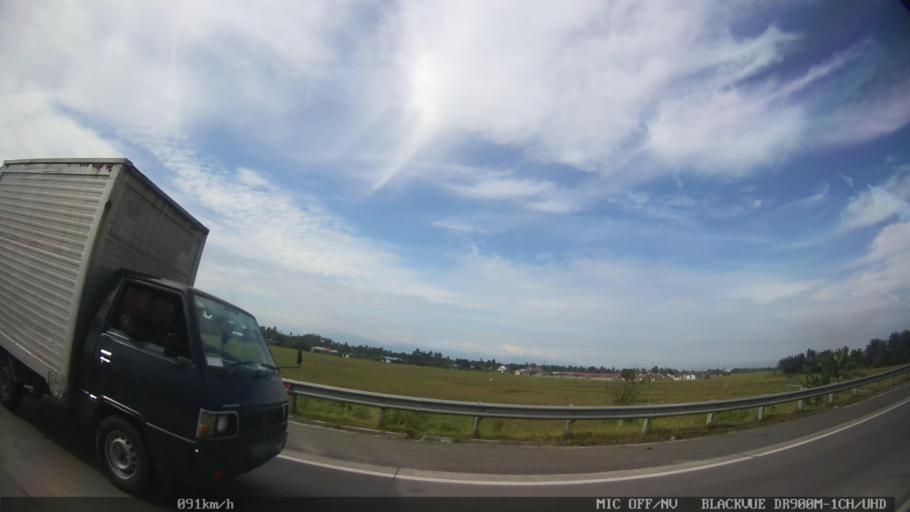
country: ID
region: North Sumatra
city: Sunggal
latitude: 3.6420
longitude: 98.5654
